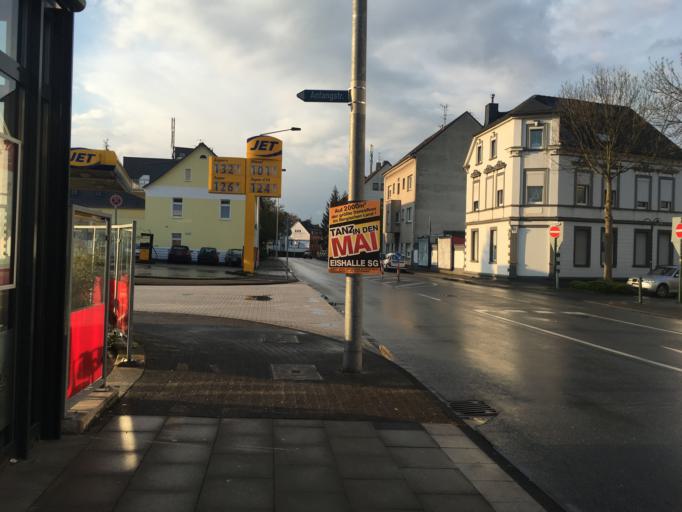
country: DE
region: North Rhine-Westphalia
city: Haan
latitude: 51.1614
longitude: 6.9944
